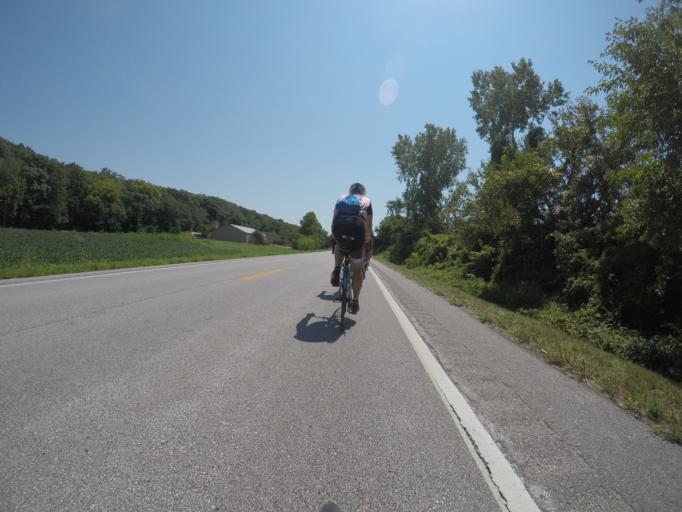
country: US
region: Kansas
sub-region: Leavenworth County
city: Leavenworth
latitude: 39.3374
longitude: -94.8609
